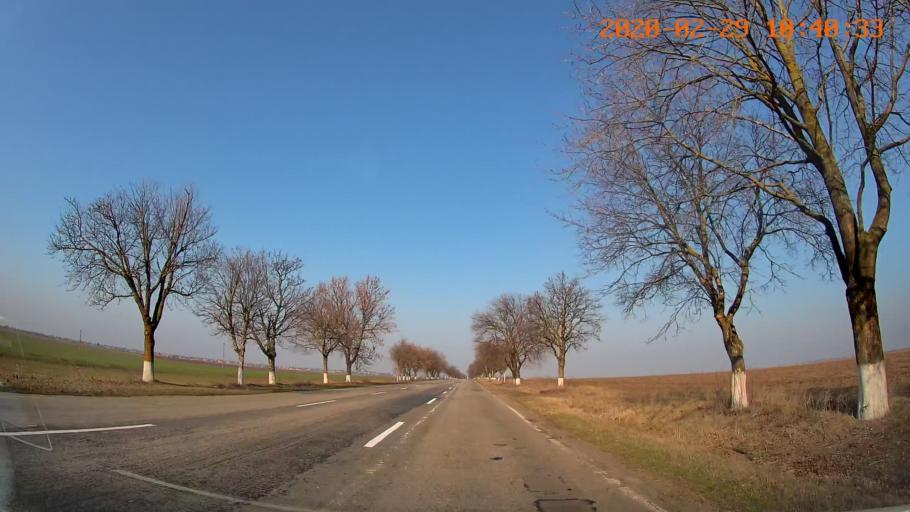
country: MD
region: Anenii Noi
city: Varnita
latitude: 47.0340
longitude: 29.4381
